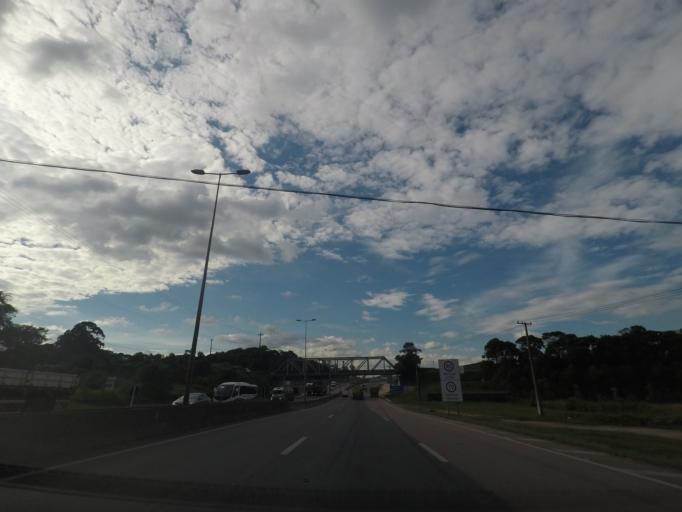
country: BR
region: Parana
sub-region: Sao Jose Dos Pinhais
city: Sao Jose dos Pinhais
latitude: -25.5630
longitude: -49.3085
